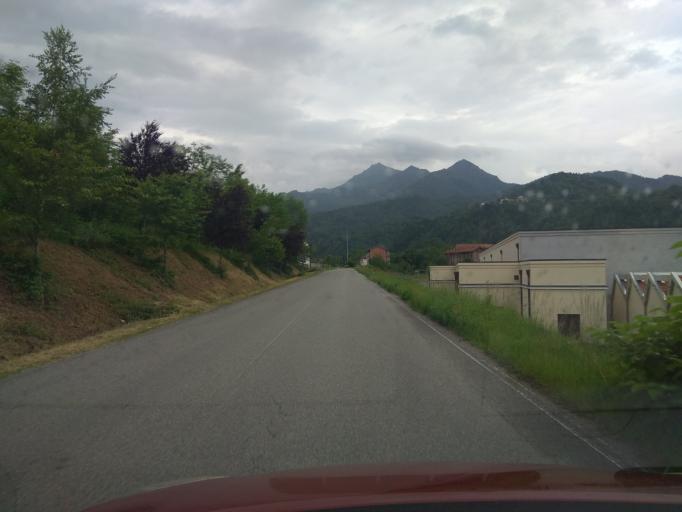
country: IT
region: Piedmont
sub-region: Provincia di Biella
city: Pray
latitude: 45.6731
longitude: 8.2010
